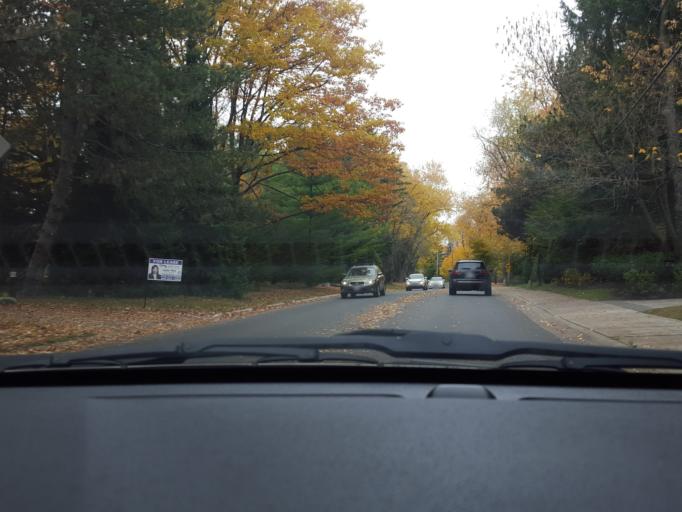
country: CA
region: Ontario
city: Willowdale
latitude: 43.7365
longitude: -79.3704
